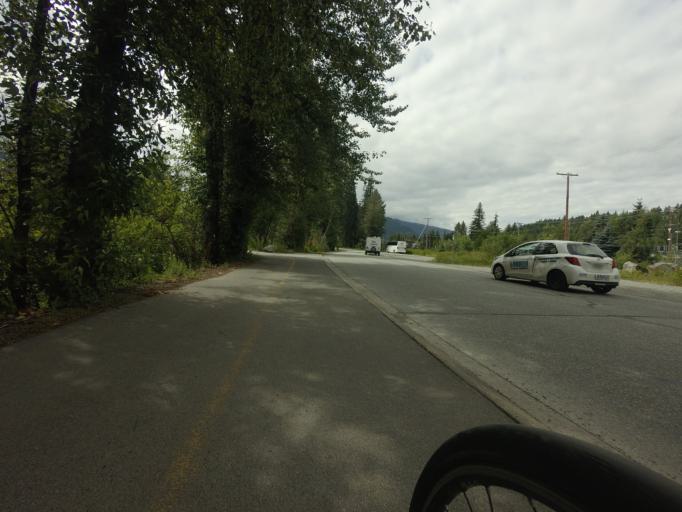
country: CA
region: British Columbia
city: Whistler
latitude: 50.1337
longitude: -122.9527
